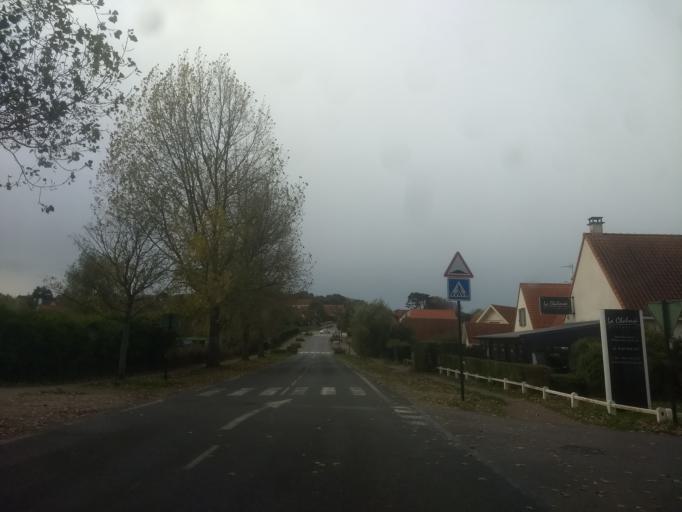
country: FR
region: Nord-Pas-de-Calais
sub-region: Departement du Pas-de-Calais
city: Wissant
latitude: 50.8856
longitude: 1.6677
